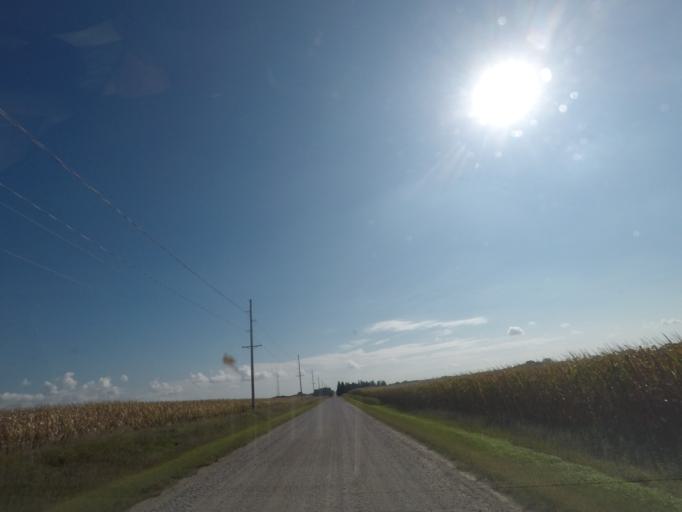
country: US
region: Iowa
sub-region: Story County
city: Nevada
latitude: 42.0347
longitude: -93.4046
